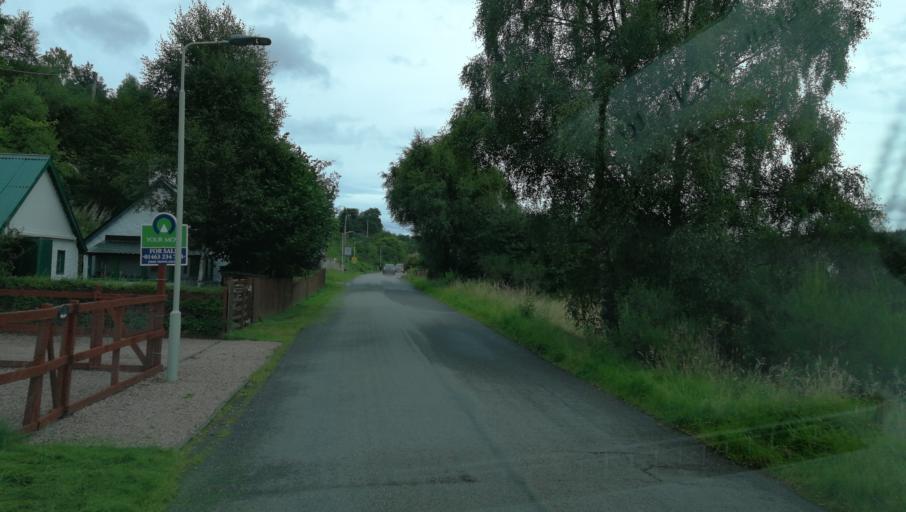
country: GB
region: Scotland
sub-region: Highland
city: Beauly
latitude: 57.3444
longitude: -4.7702
